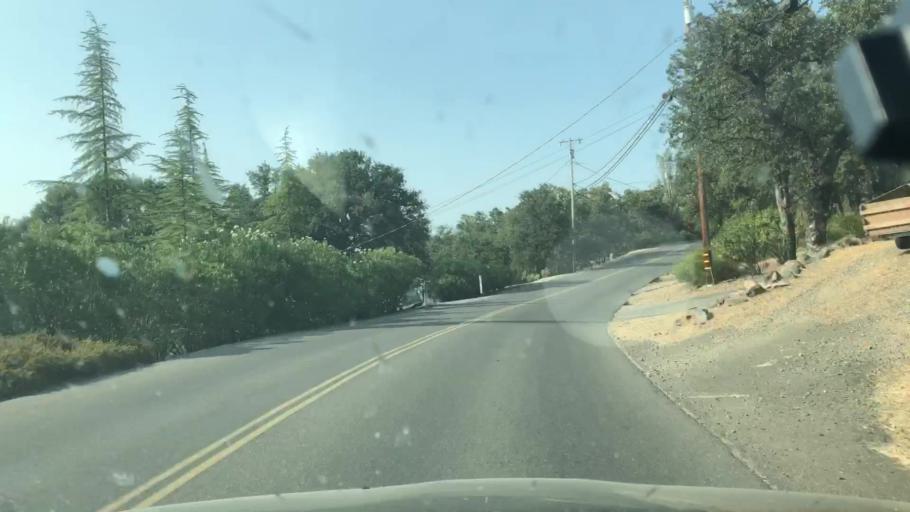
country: US
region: California
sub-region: Lake County
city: Hidden Valley Lake
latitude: 38.8057
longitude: -122.5592
